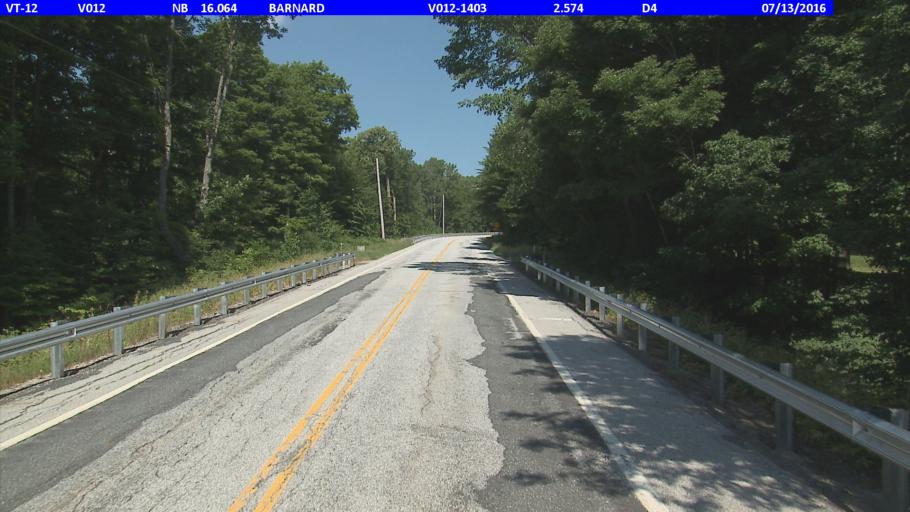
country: US
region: Vermont
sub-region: Windsor County
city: Woodstock
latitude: 43.6995
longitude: -72.6174
